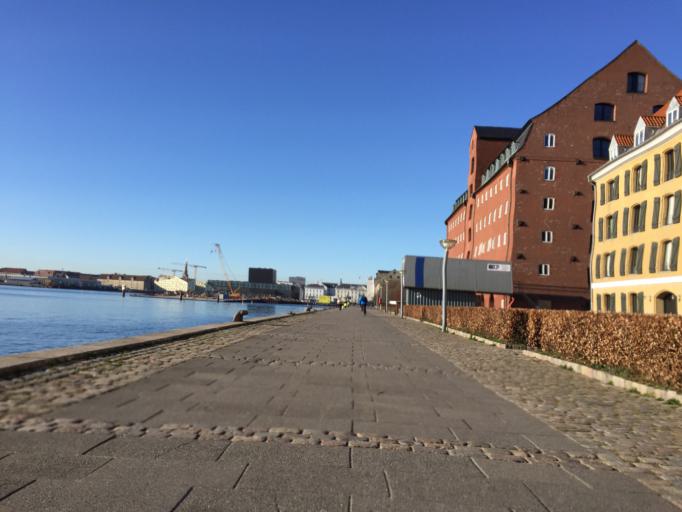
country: DK
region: Capital Region
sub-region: Kobenhavn
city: Christianshavn
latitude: 55.6856
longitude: 12.5973
